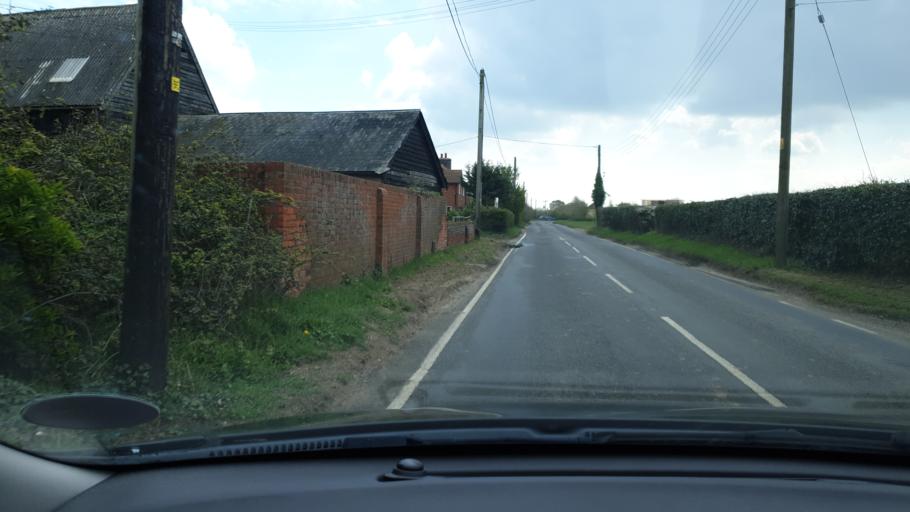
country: GB
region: England
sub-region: Essex
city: Alresford
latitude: 51.9033
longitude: 1.0101
